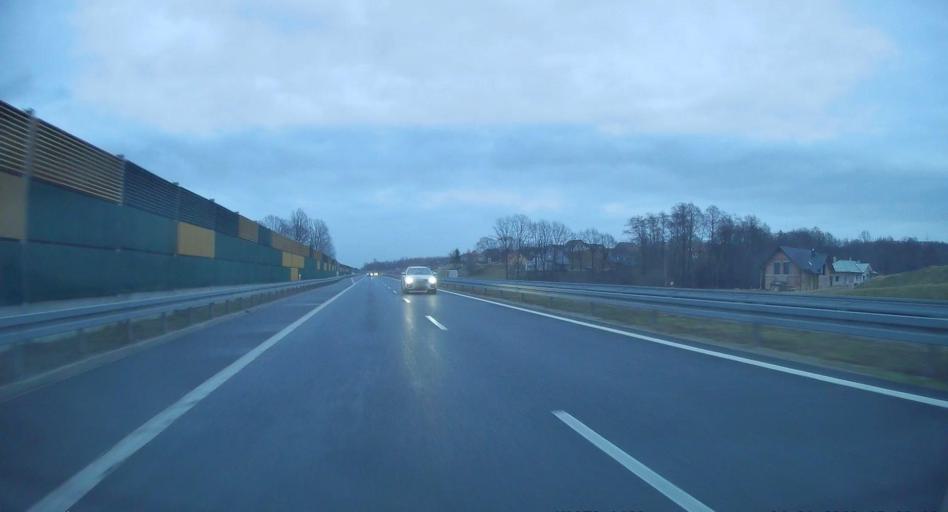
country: PL
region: Subcarpathian Voivodeship
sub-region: Powiat ropczycko-sedziszowski
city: Ropczyce
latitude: 50.0494
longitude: 21.6118
